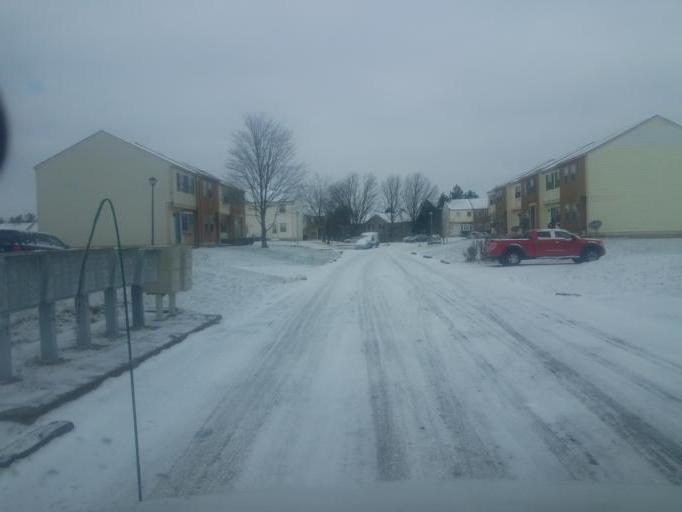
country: US
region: Ohio
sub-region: Franklin County
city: Dublin
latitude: 40.1139
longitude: -83.0865
